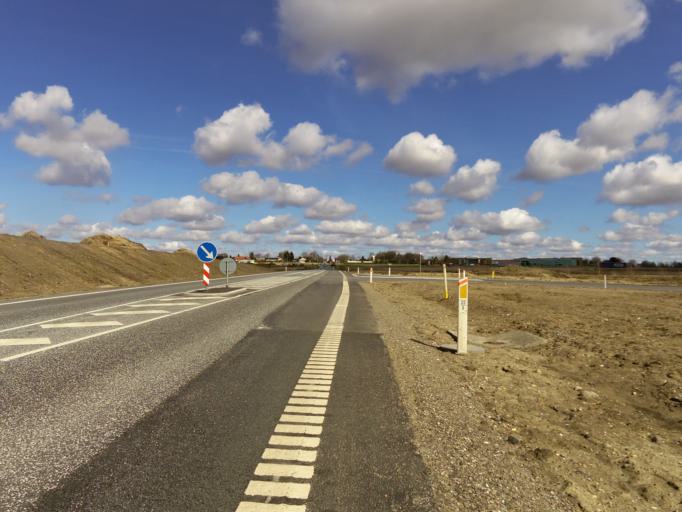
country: DK
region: South Denmark
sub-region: Tonder Kommune
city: Toftlund
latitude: 55.1771
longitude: 9.0602
